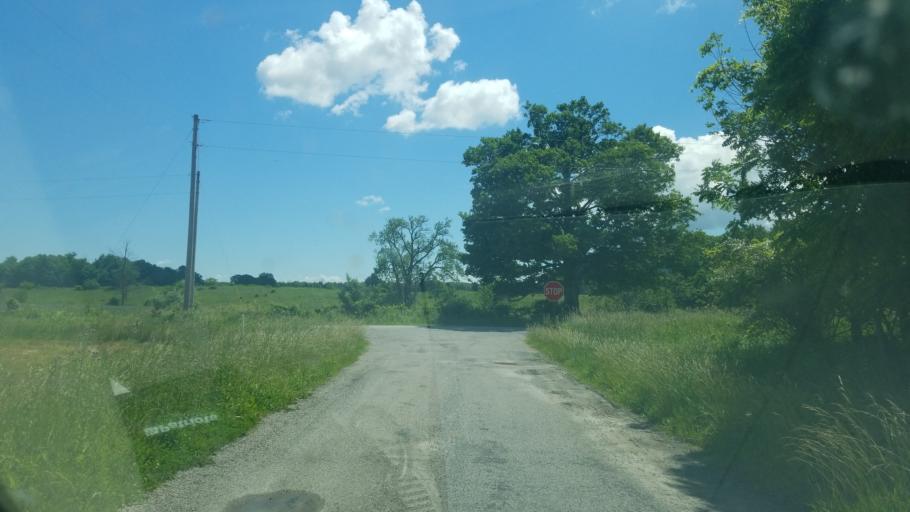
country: US
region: Ohio
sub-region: Huron County
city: New London
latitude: 41.1506
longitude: -82.3900
